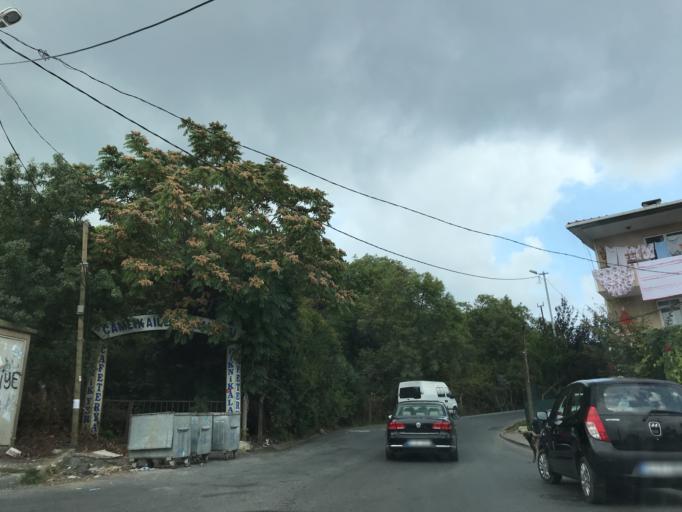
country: TR
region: Istanbul
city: Arikoey
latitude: 41.1783
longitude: 29.0491
